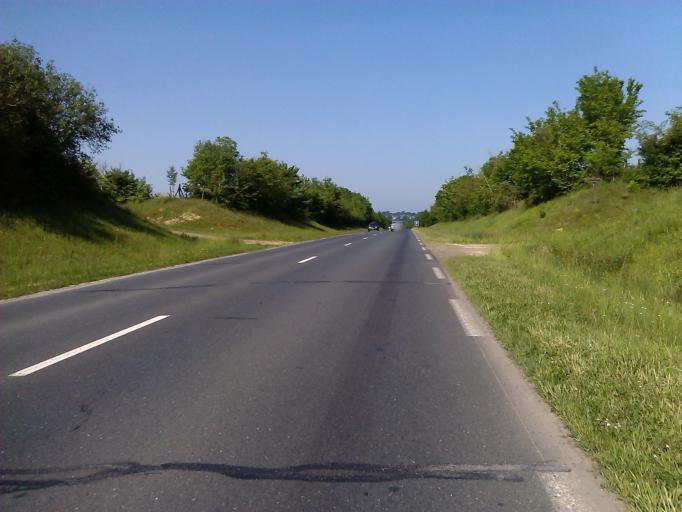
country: FR
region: Centre
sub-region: Departement de l'Indre
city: Neuvy-Saint-Sepulchre
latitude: 46.5992
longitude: 1.7587
